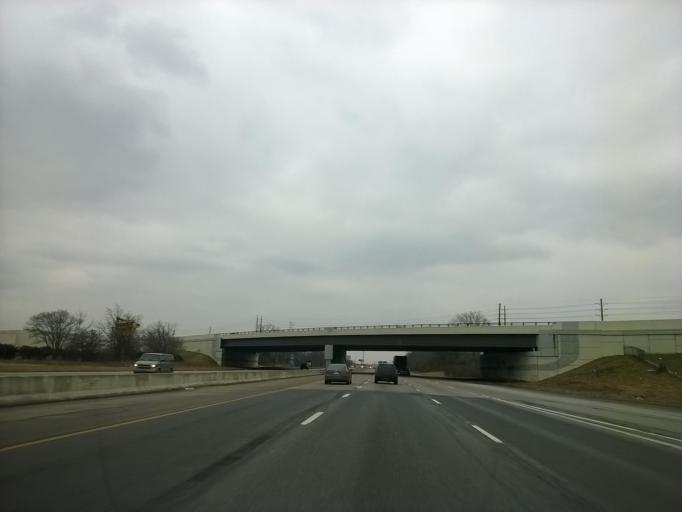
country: US
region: Indiana
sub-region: Hamilton County
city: Fishers
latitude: 39.9060
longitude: -86.0717
